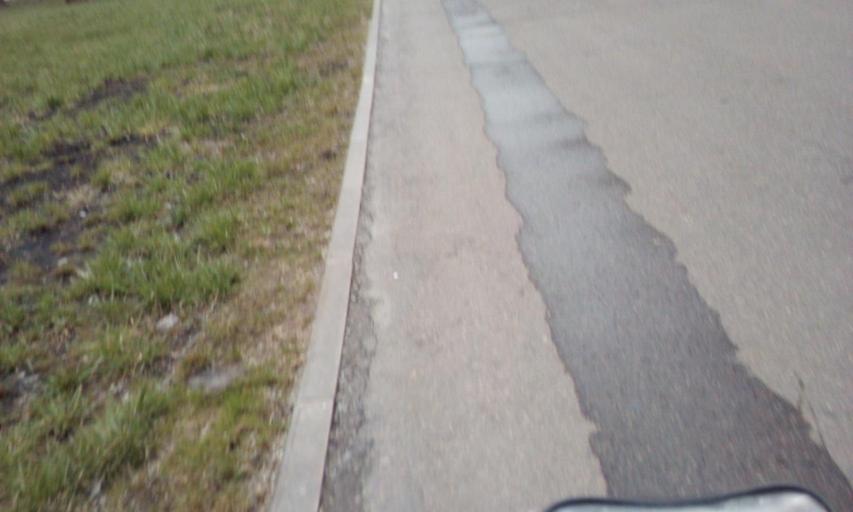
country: RU
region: Moskovskaya
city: Kommunarka
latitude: 55.5398
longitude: 37.5235
